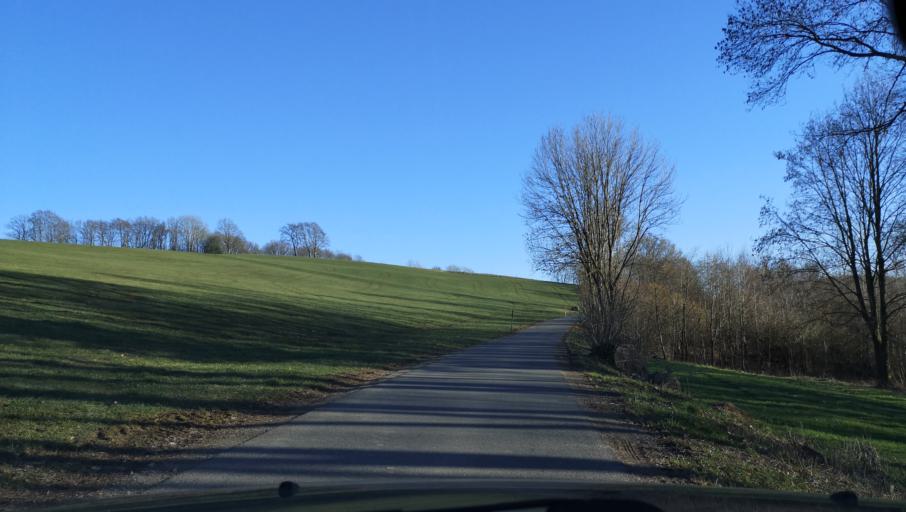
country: DE
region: North Rhine-Westphalia
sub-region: Regierungsbezirk Arnsberg
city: Breckerfeld
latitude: 51.2208
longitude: 7.4222
